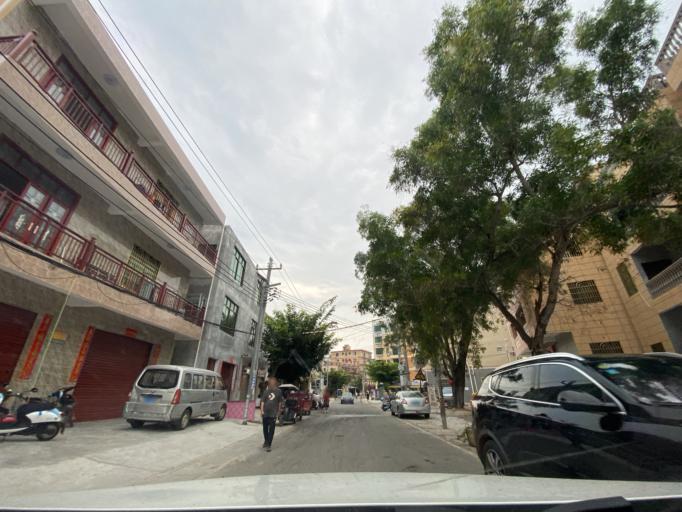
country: CN
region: Hainan
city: Yingzhou
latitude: 18.3936
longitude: 109.8438
